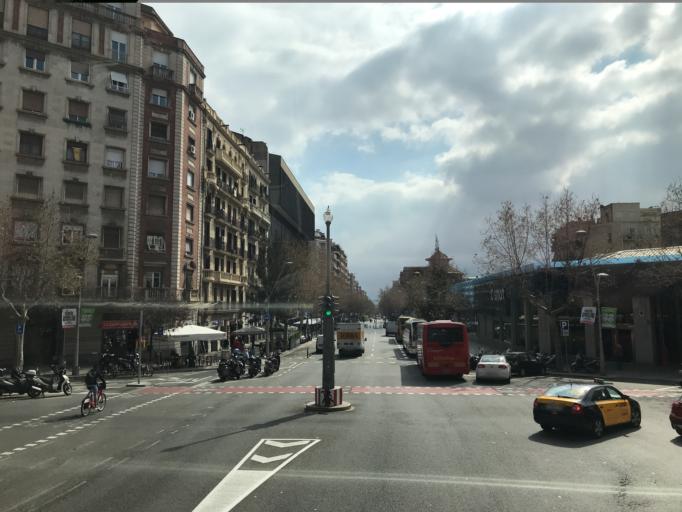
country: ES
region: Catalonia
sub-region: Provincia de Barcelona
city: Barcelona
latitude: 41.3909
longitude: 2.1469
